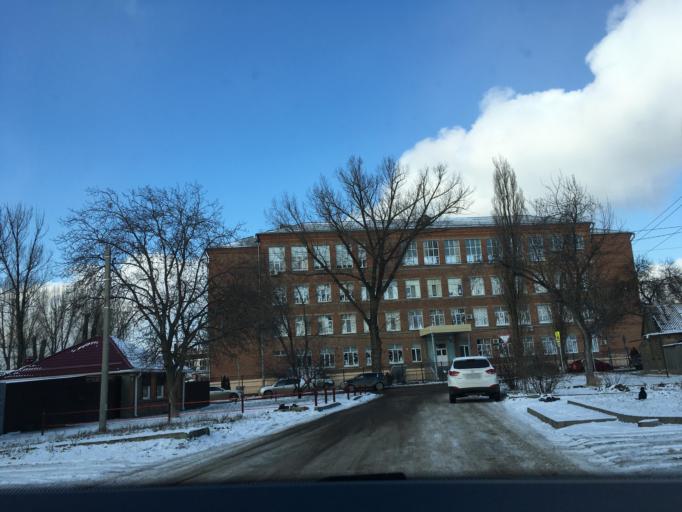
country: RU
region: Rostov
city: Rostov-na-Donu
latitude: 47.2345
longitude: 39.6349
